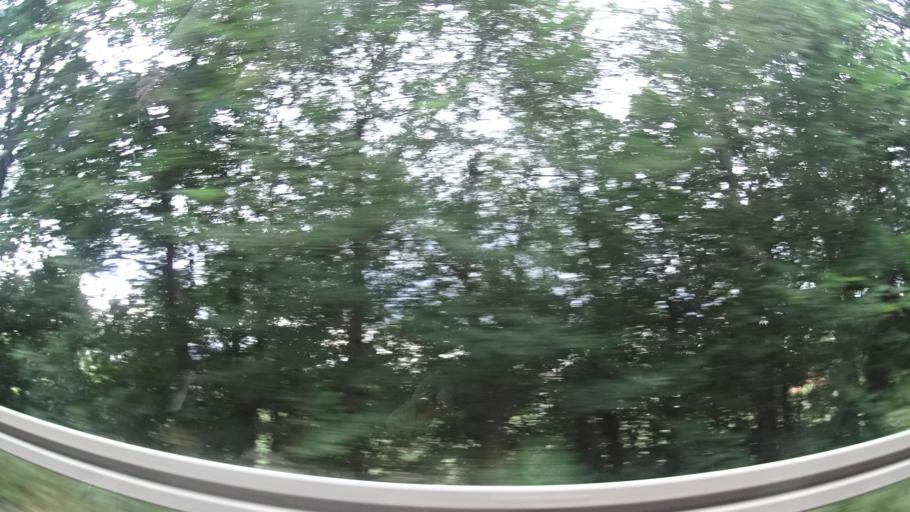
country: DE
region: Lower Saxony
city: Elze
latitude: 52.1638
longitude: 9.7124
